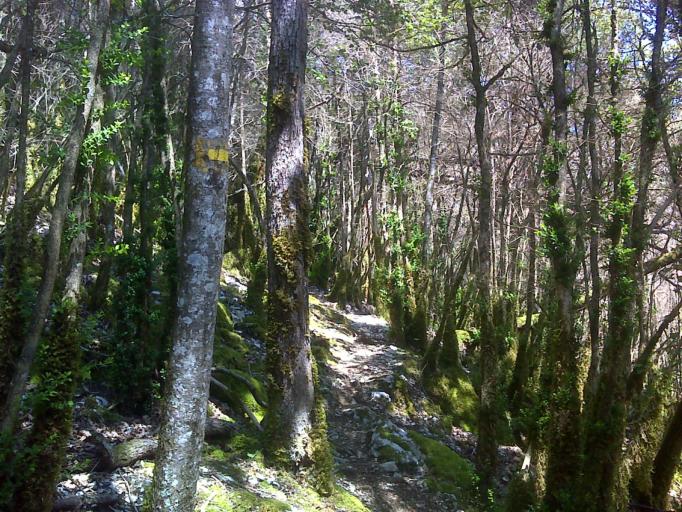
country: FR
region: Rhone-Alpes
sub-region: Departement de l'Ain
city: Montreal-la-Cluse
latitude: 46.1699
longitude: 5.6001
